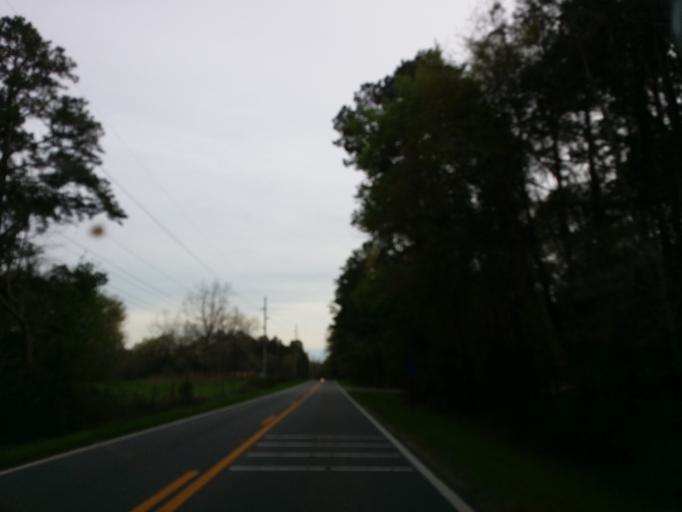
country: US
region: Florida
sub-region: Leon County
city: Tallahassee
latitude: 30.5204
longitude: -84.1299
